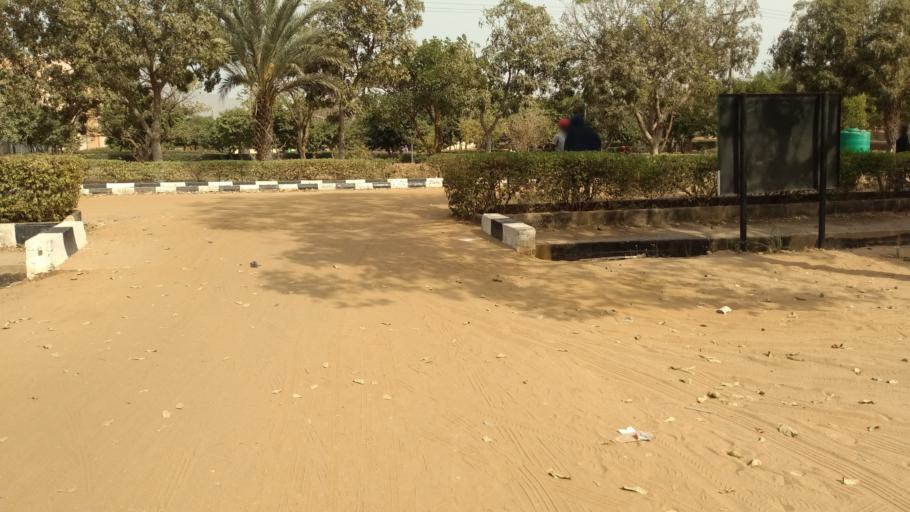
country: NG
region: Gombe
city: Gombe
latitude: 10.3068
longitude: 11.1748
